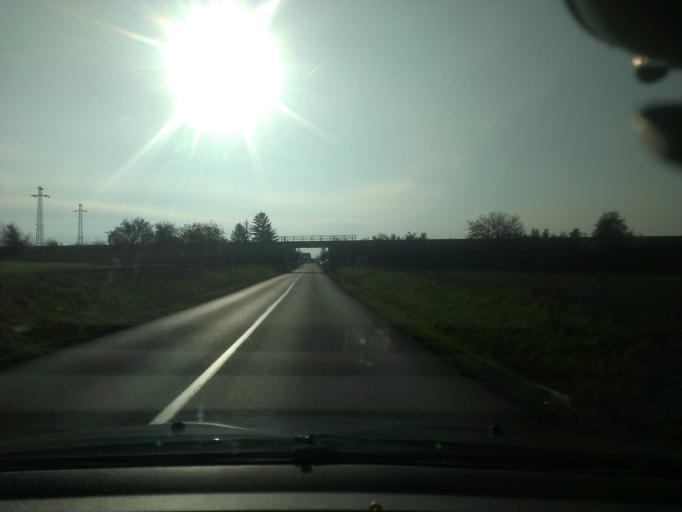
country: SK
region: Nitriansky
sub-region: Okres Nitra
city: Nitra
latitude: 48.3762
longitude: 18.0227
